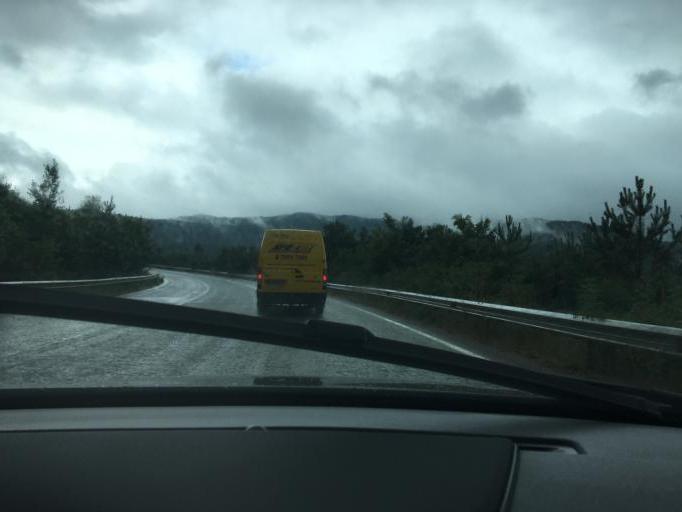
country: BG
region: Kyustendil
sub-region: Obshtina Kyustendil
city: Kyustendil
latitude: 42.2659
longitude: 22.5831
